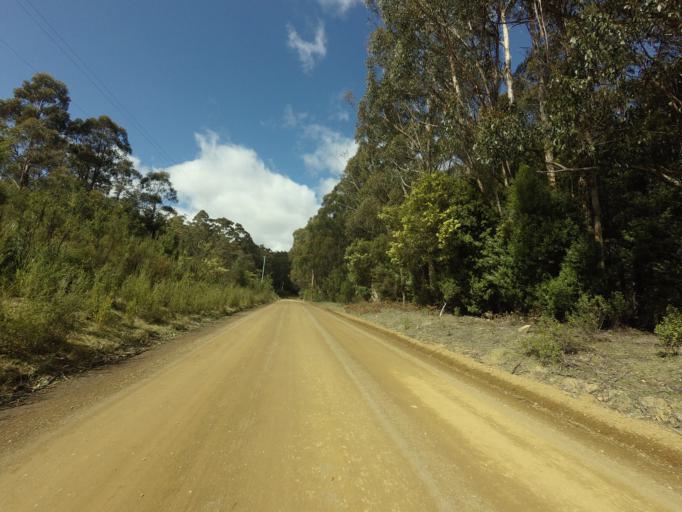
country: AU
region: Tasmania
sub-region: Huon Valley
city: Geeveston
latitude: -43.4141
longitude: 146.9051
